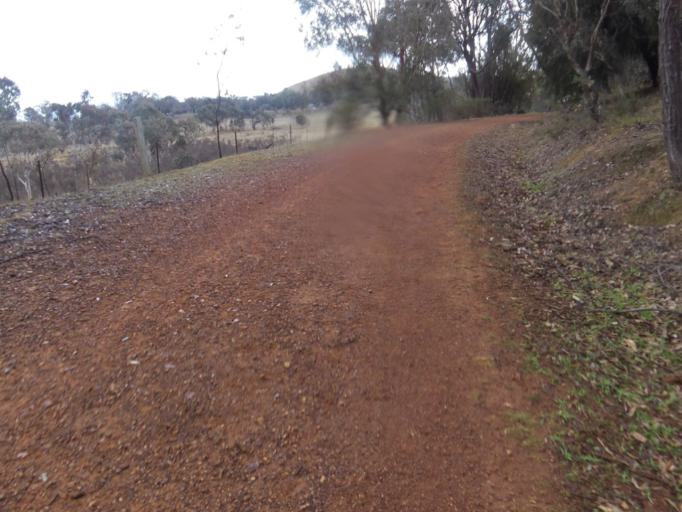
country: AU
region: Australian Capital Territory
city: Macquarie
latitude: -35.2728
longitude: 149.0798
